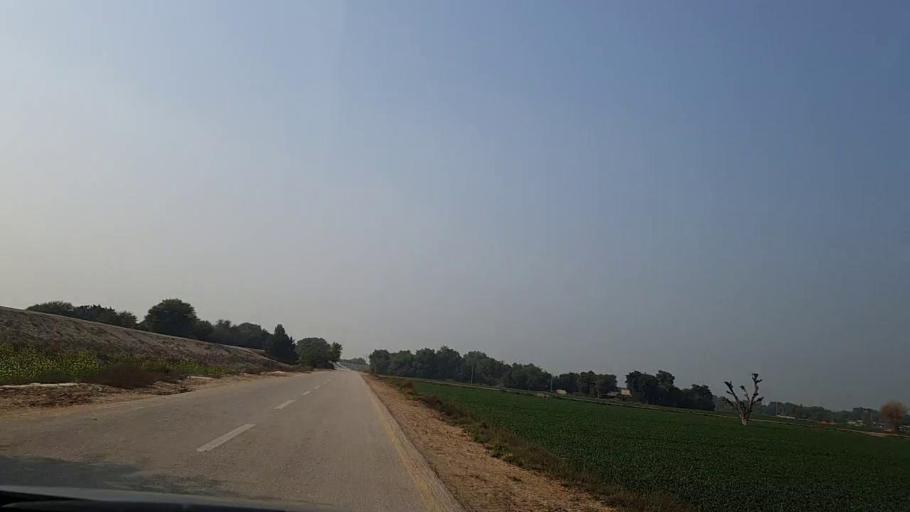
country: PK
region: Sindh
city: Sann
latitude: 26.1513
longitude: 68.1247
